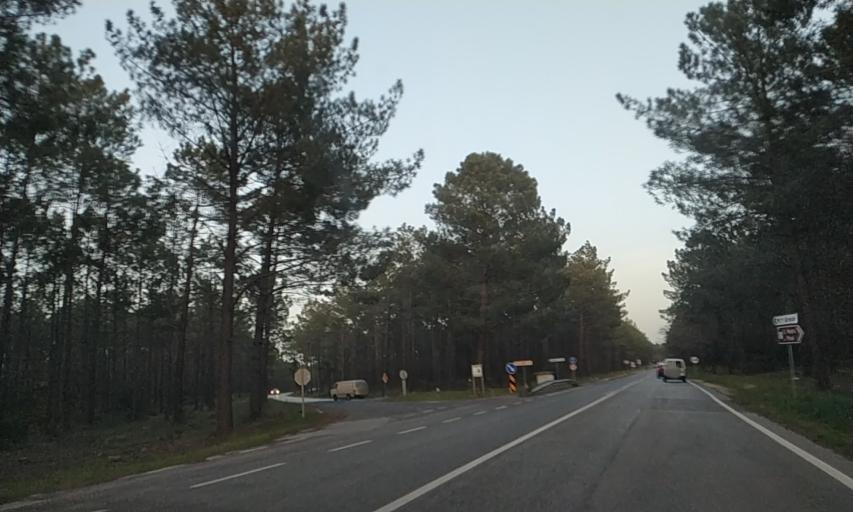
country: PT
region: Leiria
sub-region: Marinha Grande
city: Marinha Grande
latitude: 39.7473
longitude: -8.9565
